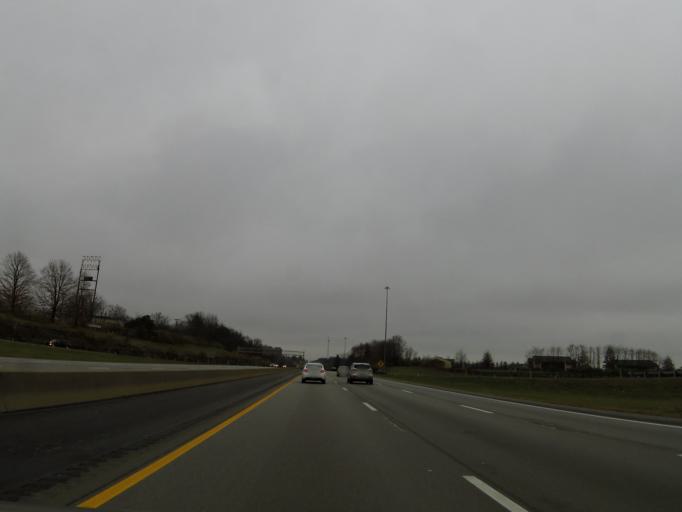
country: US
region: Kentucky
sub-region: Scott County
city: Georgetown
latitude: 38.2151
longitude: -84.5342
